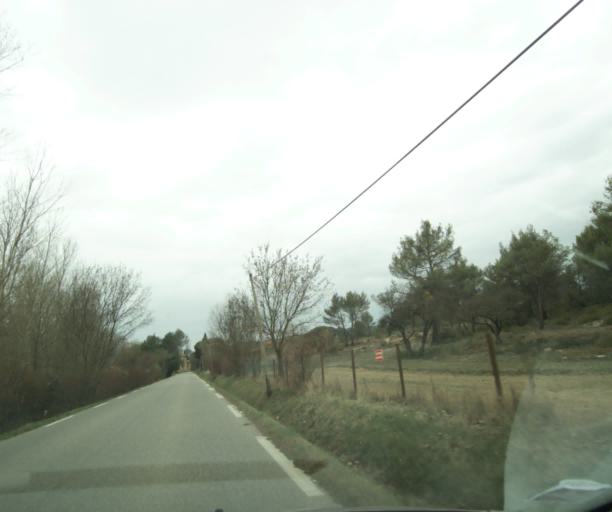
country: FR
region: Provence-Alpes-Cote d'Azur
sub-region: Departement des Bouches-du-Rhone
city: Jouques
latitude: 43.6300
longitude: 5.6585
